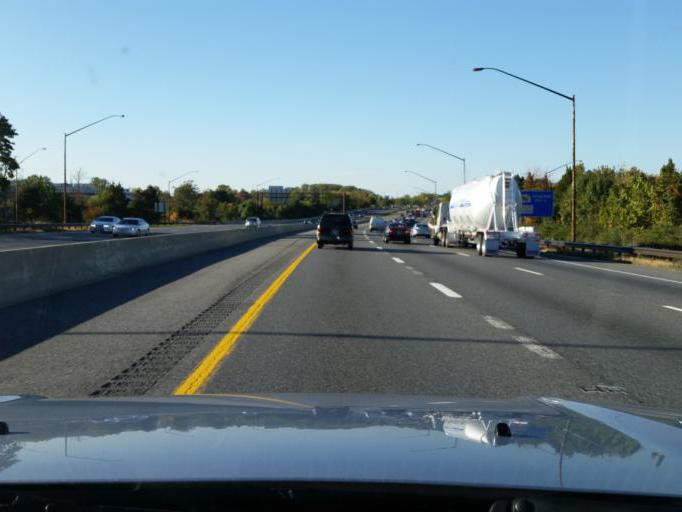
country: US
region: Maryland
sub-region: Montgomery County
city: Germantown
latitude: 39.1861
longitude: -77.2562
